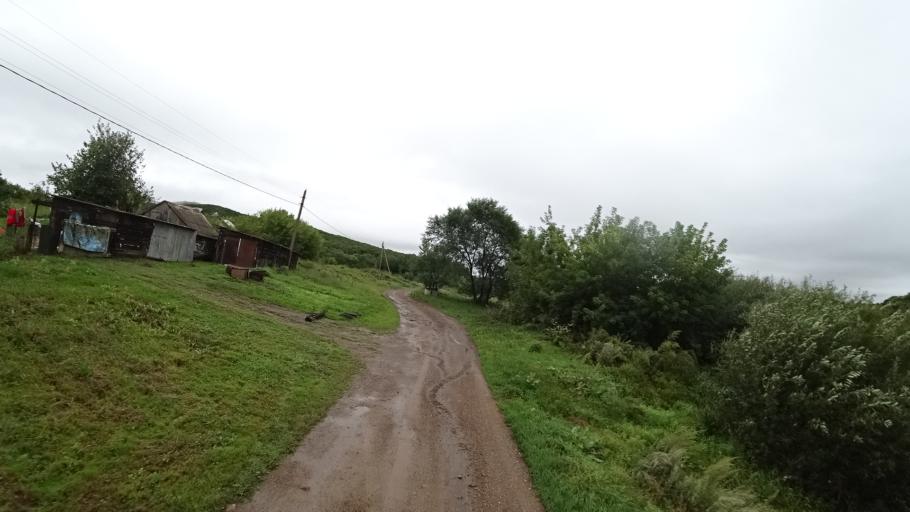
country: RU
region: Primorskiy
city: Monastyrishche
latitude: 44.2728
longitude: 132.4054
